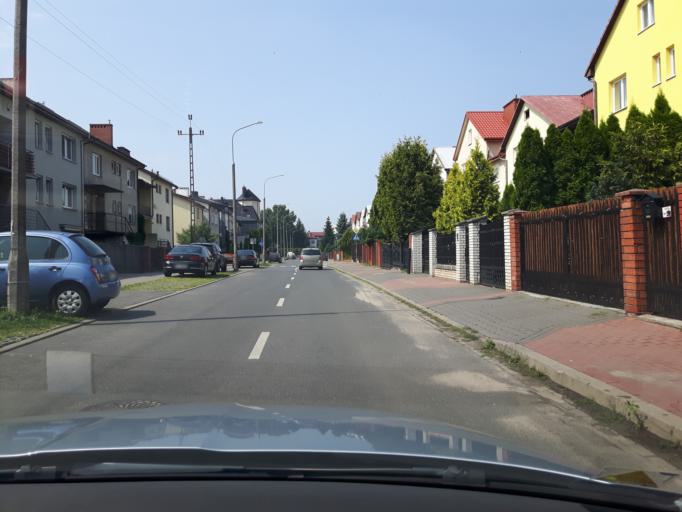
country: PL
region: Masovian Voivodeship
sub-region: Powiat wolominski
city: Zabki
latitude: 52.2962
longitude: 21.0927
